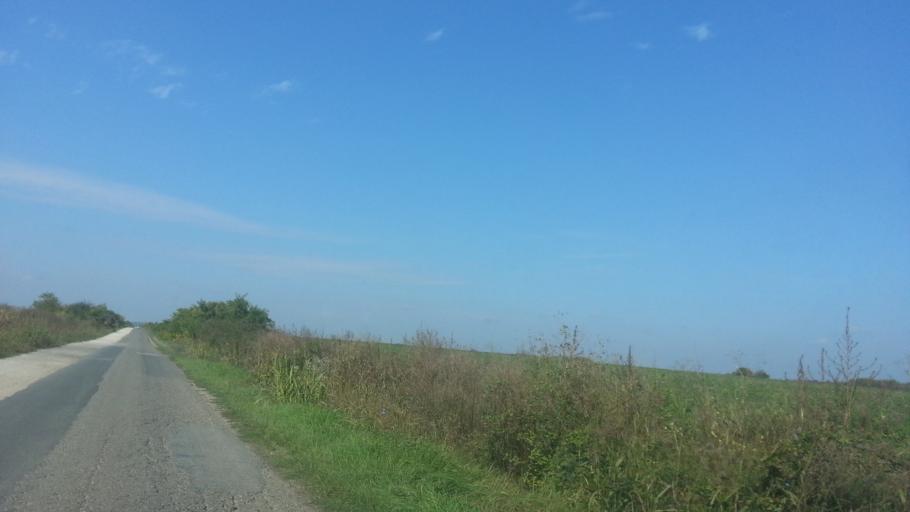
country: RS
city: Surduk
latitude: 45.1003
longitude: 20.2894
